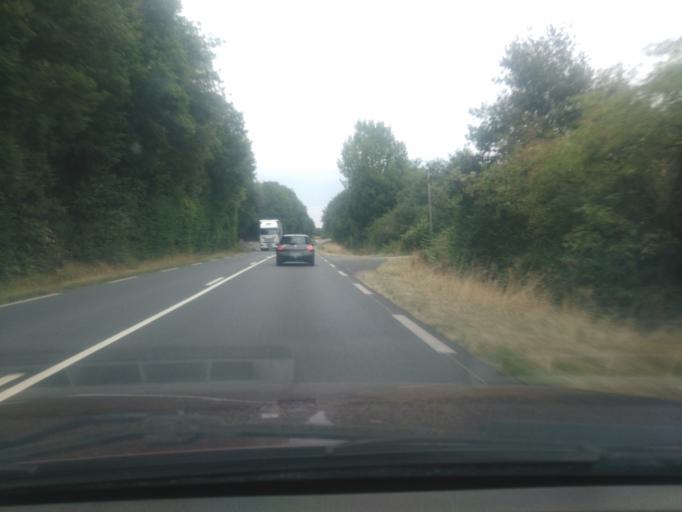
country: FR
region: Centre
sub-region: Departement de l'Indre
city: Belabre
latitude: 46.6288
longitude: 1.1996
